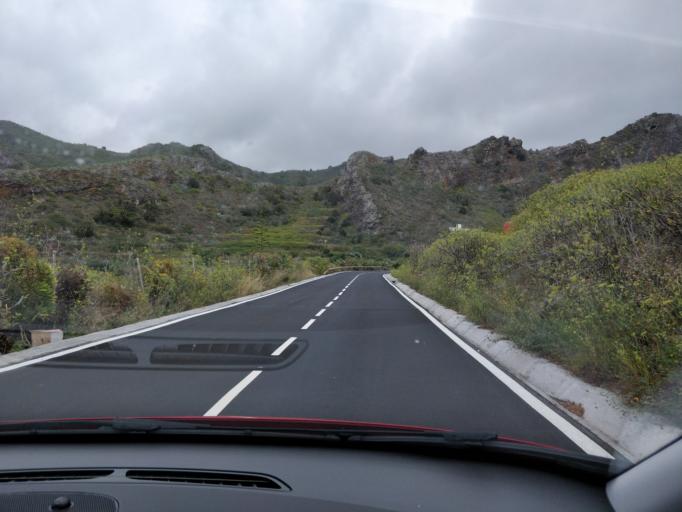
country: ES
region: Canary Islands
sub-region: Provincia de Santa Cruz de Tenerife
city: Tanque
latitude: 28.3485
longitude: -16.8445
